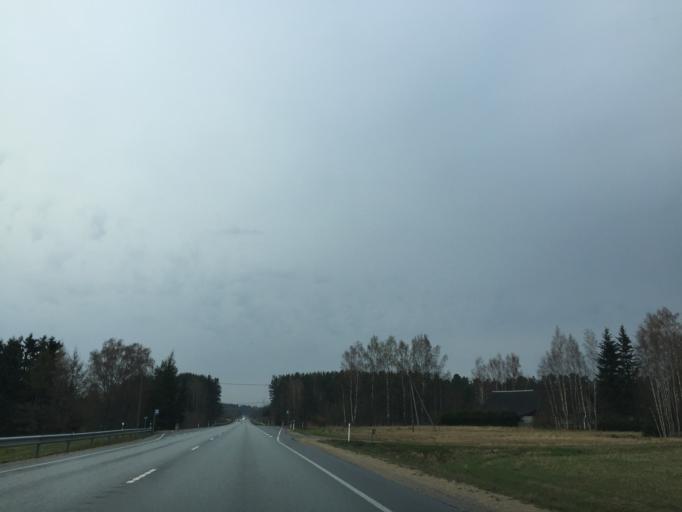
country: EE
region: Tartu
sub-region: UElenurme vald
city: Ulenurme
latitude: 58.2102
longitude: 26.7067
